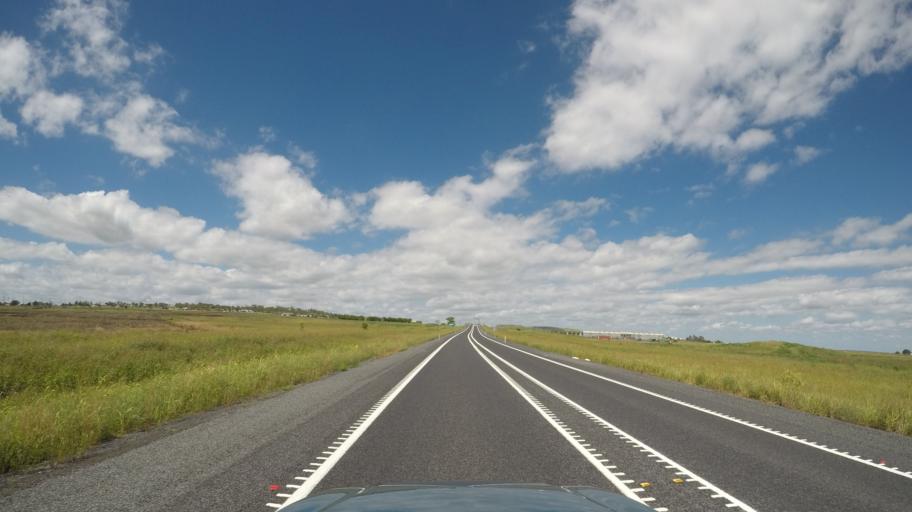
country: AU
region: Queensland
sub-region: Toowoomba
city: Wilsonton Heights
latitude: -27.5337
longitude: 151.8524
